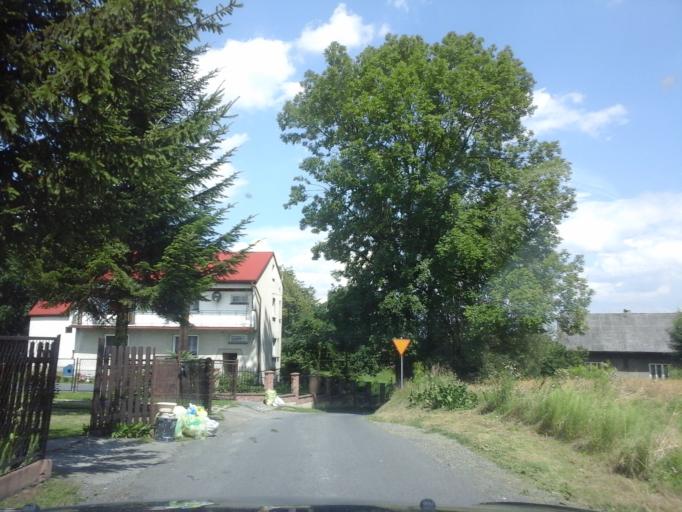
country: PL
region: Lesser Poland Voivodeship
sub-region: Powiat wadowicki
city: Ryczow
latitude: 49.9793
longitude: 19.5625
